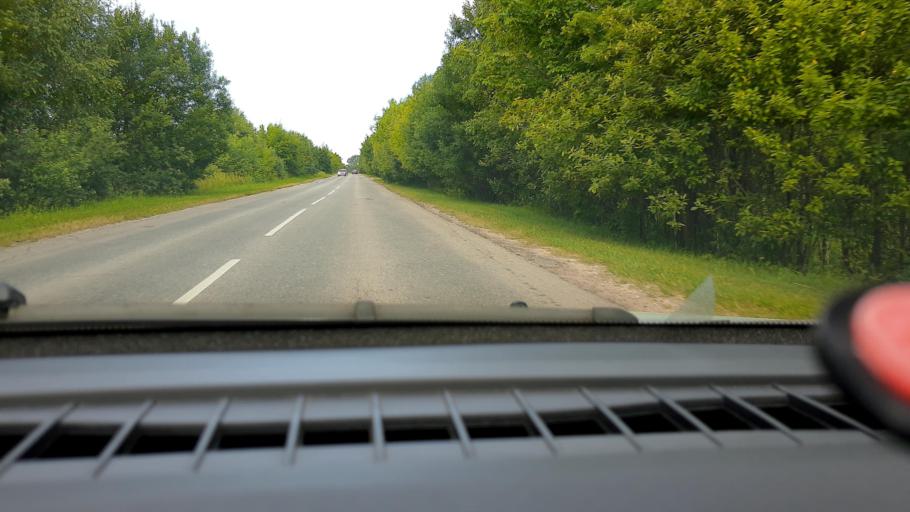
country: RU
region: Nizjnij Novgorod
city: Kstovo
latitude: 56.1488
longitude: 44.3065
